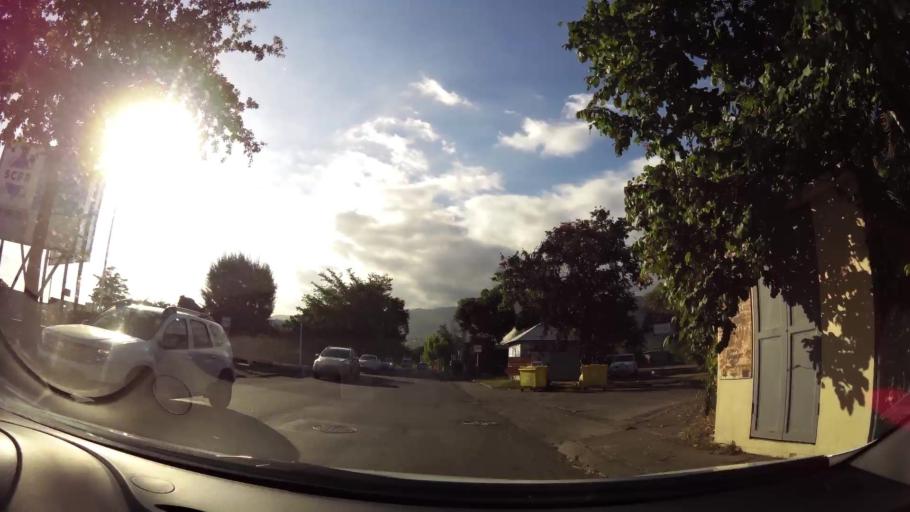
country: RE
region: Reunion
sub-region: Reunion
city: Saint-Louis
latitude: -21.2771
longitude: 55.3732
